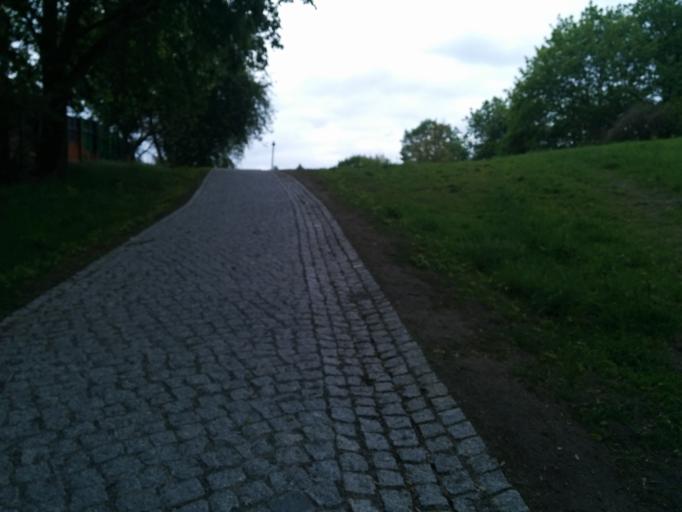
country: DE
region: Berlin
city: Hermsdorf
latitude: 52.6177
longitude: 13.3210
